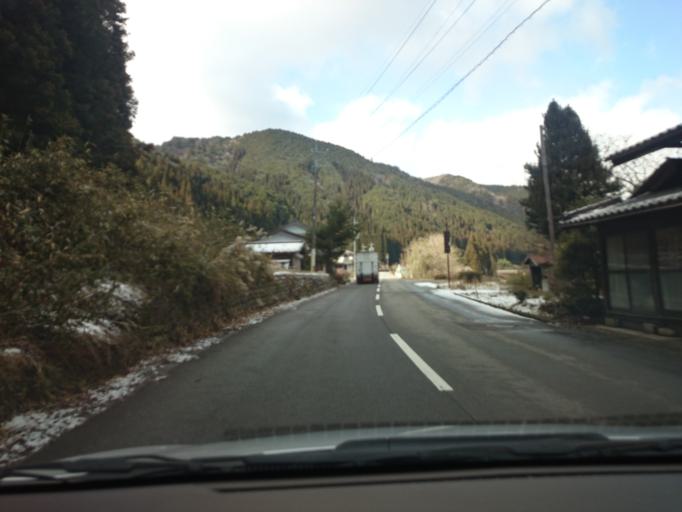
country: JP
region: Gifu
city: Gujo
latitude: 35.7407
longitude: 137.1132
